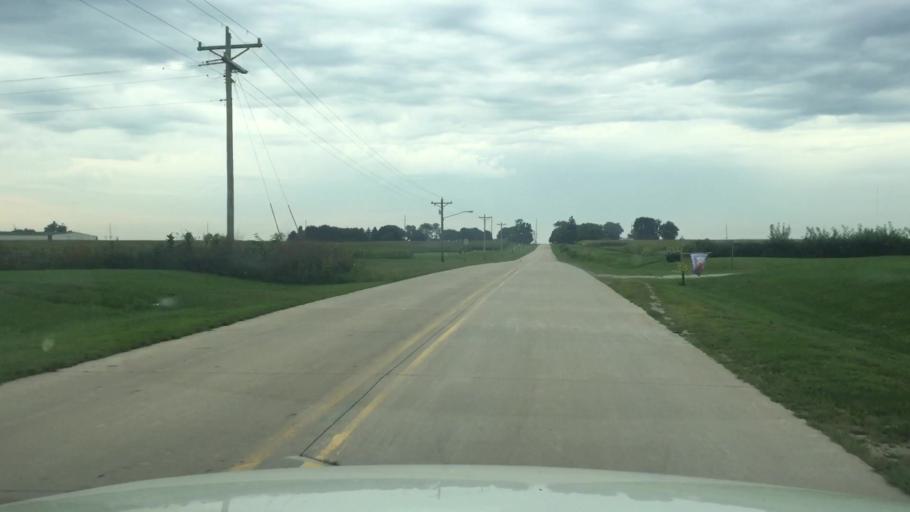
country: US
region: Iowa
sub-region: Story County
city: Huxley
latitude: 41.8853
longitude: -93.5809
